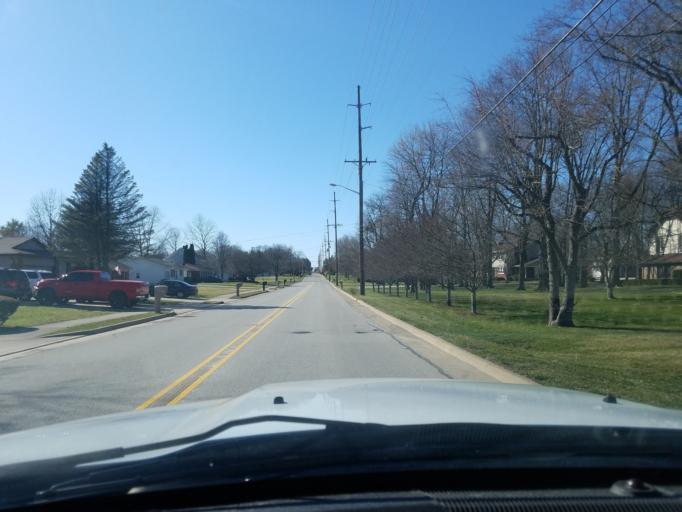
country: US
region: Indiana
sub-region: Shelby County
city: Shelbyville
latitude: 39.5045
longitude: -85.7637
